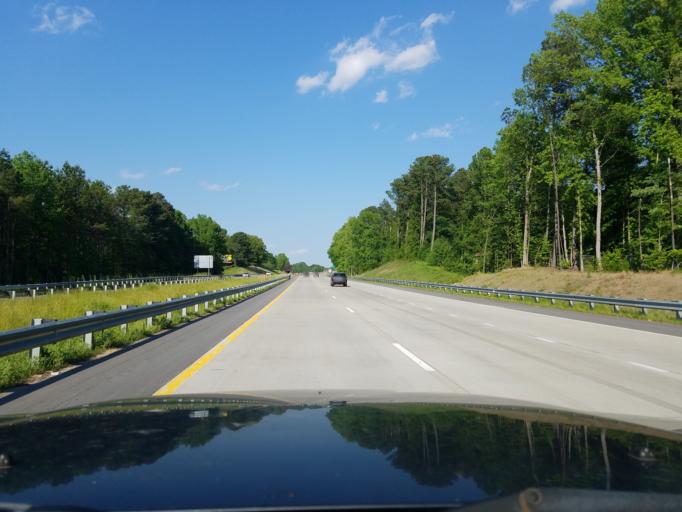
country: US
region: North Carolina
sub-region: Vance County
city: Henderson
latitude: 36.3420
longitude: -78.4057
